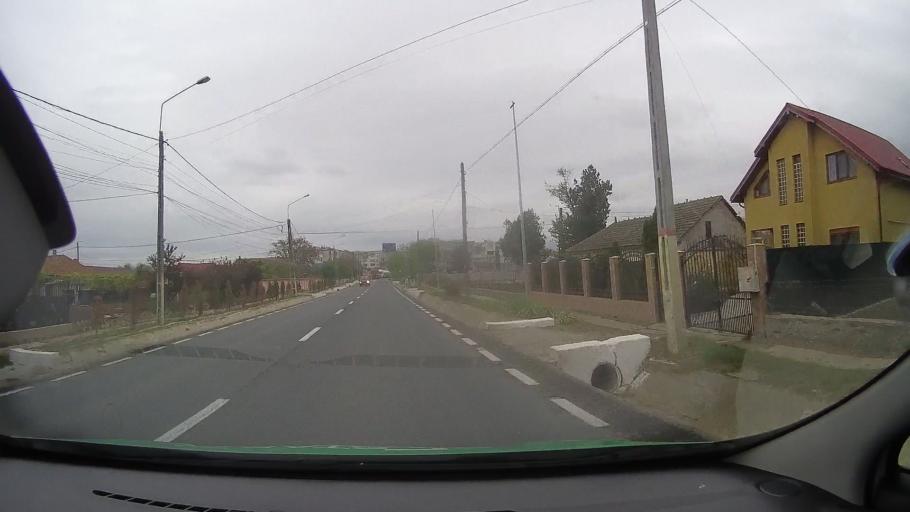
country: RO
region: Constanta
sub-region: Comuna Mihail Kogalniceanu
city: Mihail Kogalniceanu
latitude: 44.3673
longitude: 28.4588
